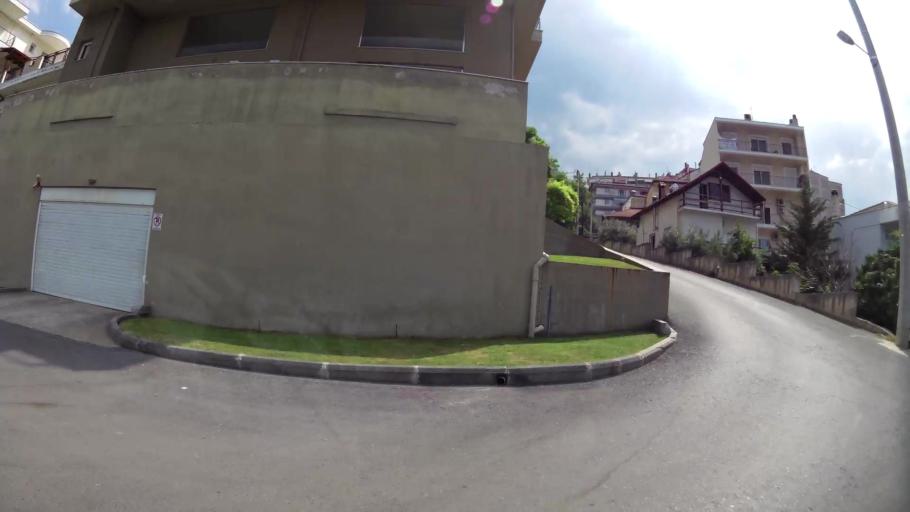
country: GR
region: Central Macedonia
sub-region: Nomos Imathias
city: Veroia
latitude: 40.5145
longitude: 22.2102
